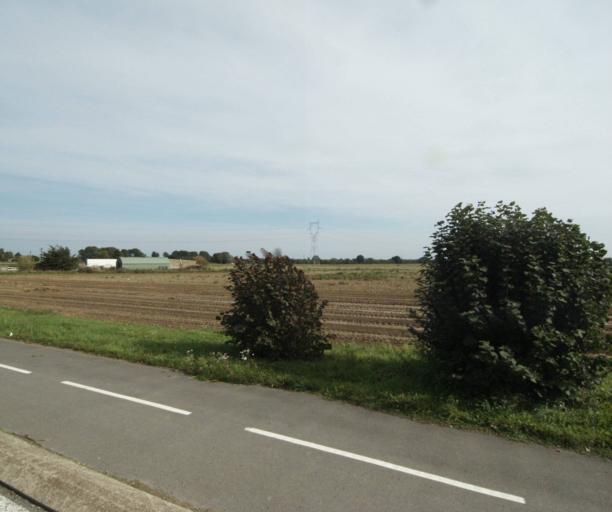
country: FR
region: Nord-Pas-de-Calais
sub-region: Departement du Nord
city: Radinghem-en-Weppes
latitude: 50.6105
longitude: 2.9221
